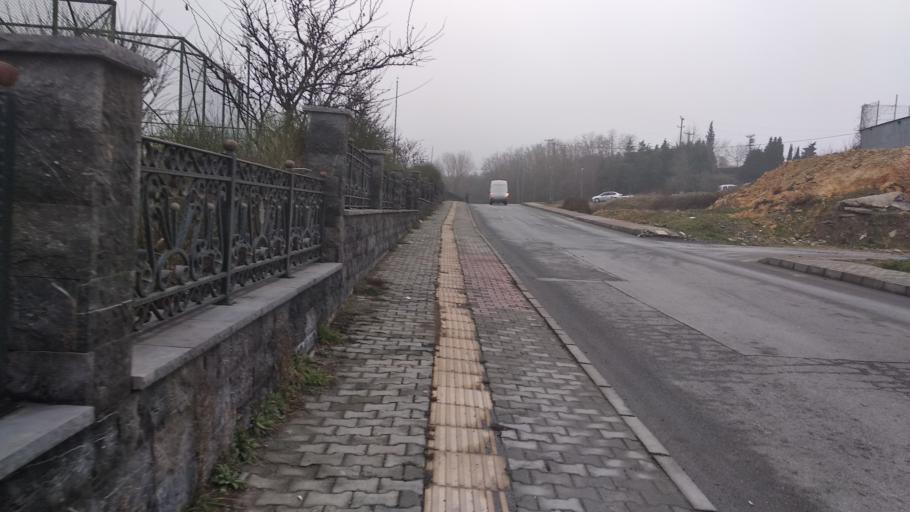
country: TR
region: Istanbul
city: Basaksehir
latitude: 41.1797
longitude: 28.7474
